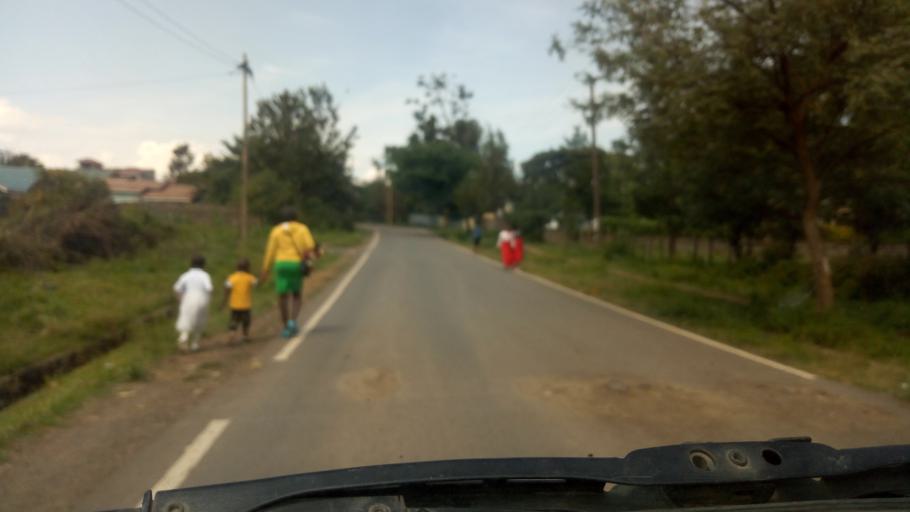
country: KE
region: Nakuru
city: Nakuru
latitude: -0.2782
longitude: 36.1030
